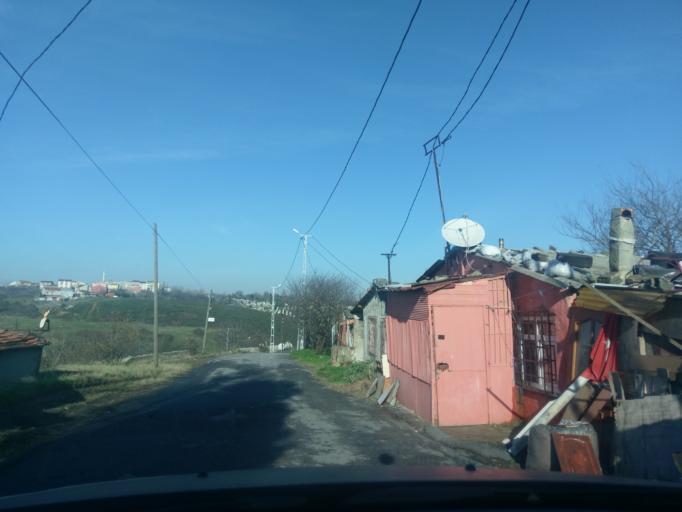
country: TR
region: Istanbul
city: Sultangazi
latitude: 41.1356
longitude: 28.8425
